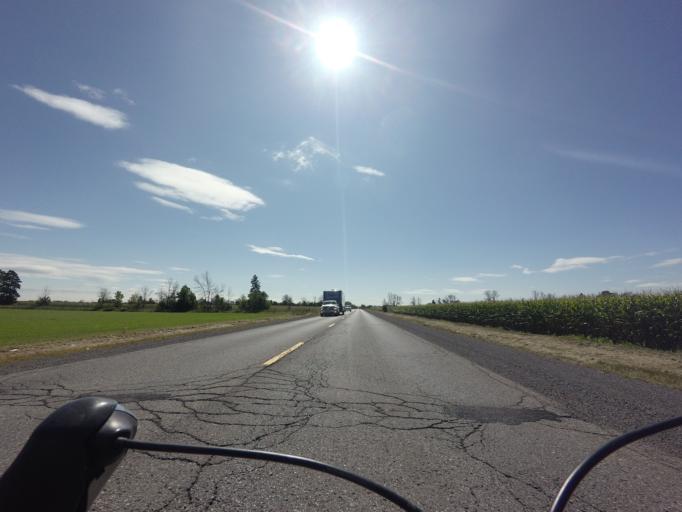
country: CA
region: Ontario
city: Bells Corners
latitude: 45.2161
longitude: -75.8290
